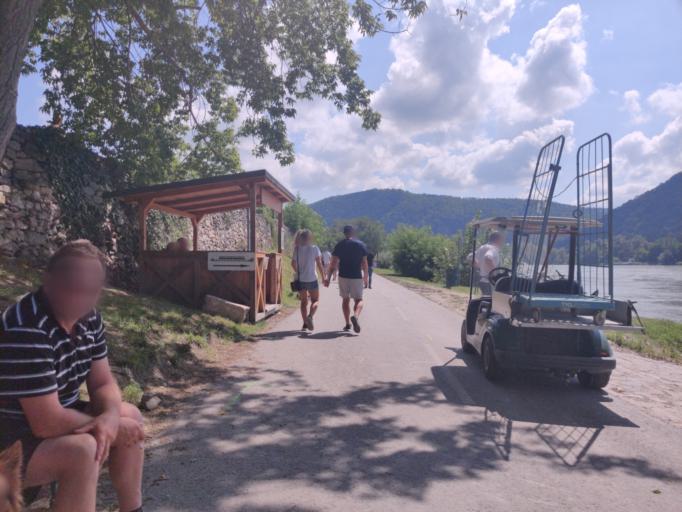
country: AT
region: Lower Austria
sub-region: Politischer Bezirk Krems
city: Durnstein
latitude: 48.3934
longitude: 15.5199
